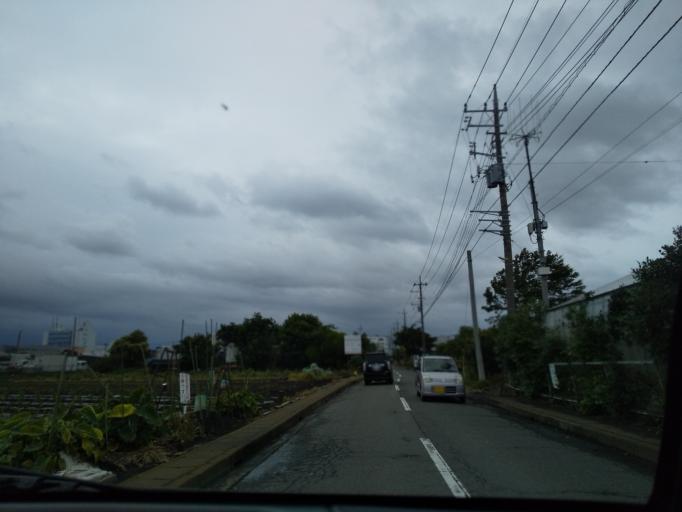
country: JP
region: Kanagawa
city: Minami-rinkan
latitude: 35.4369
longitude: 139.4428
